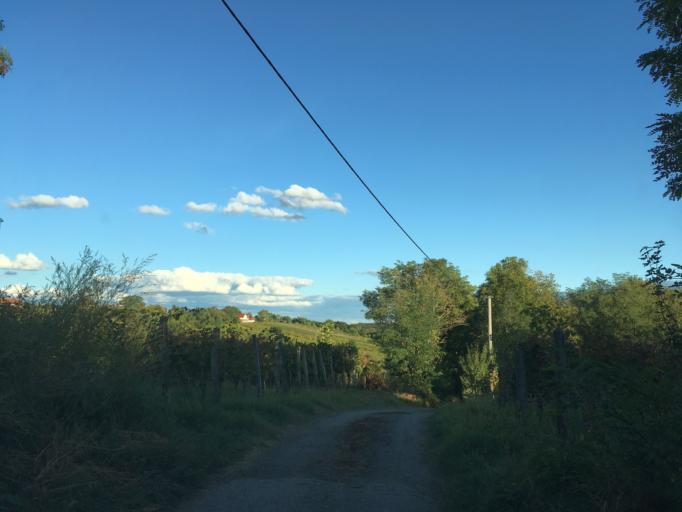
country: SK
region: Nitriansky
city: Svodin
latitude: 47.9162
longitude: 18.4345
